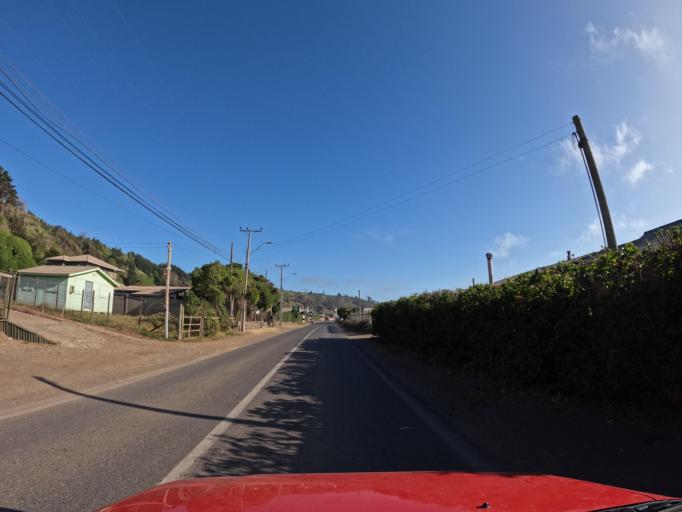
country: CL
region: Maule
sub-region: Provincia de Talca
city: Constitucion
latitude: -34.8980
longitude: -72.1794
